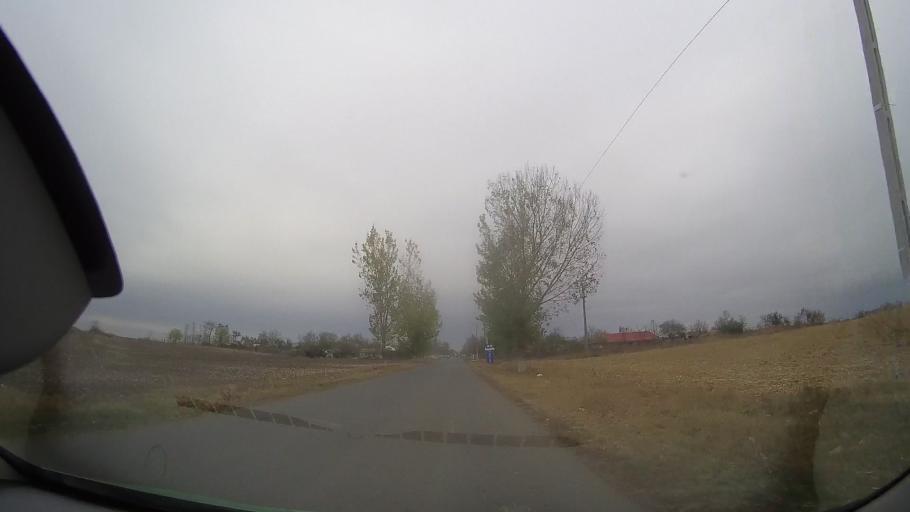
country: RO
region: Braila
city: Dudesti
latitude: 44.8730
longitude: 27.4296
